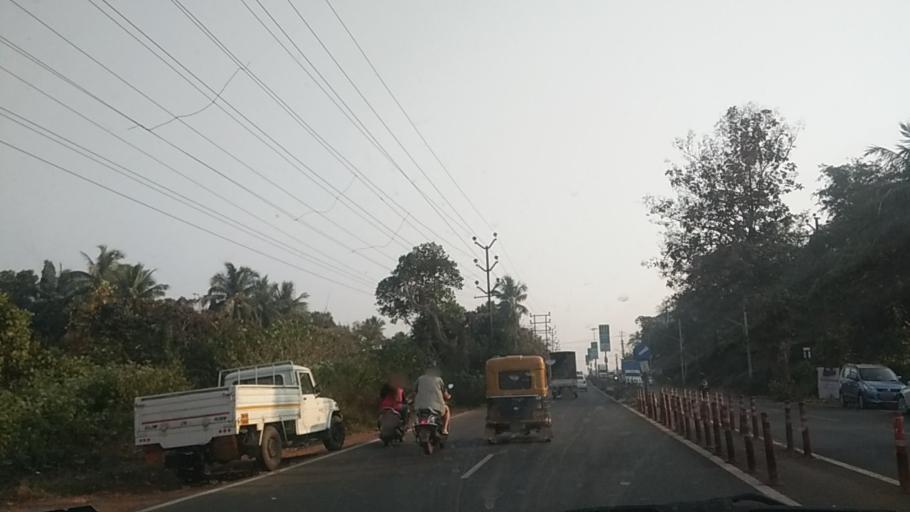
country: IN
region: Goa
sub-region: North Goa
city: Serula
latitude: 15.5336
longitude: 73.8241
